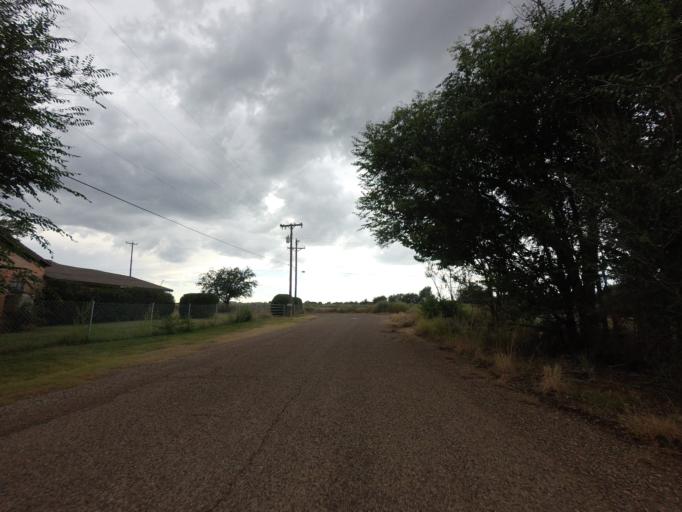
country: US
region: New Mexico
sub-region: Curry County
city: Clovis
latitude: 34.3878
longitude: -103.1870
